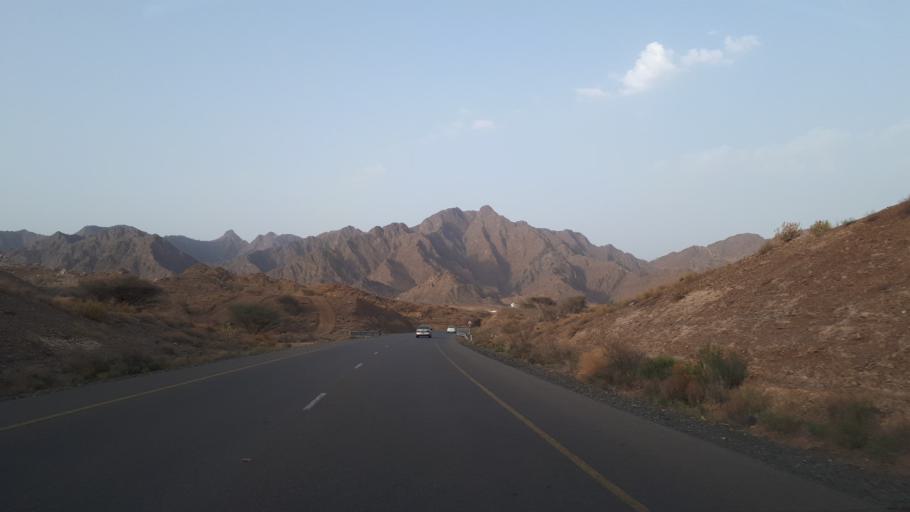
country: OM
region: Al Batinah
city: Rustaq
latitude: 23.4306
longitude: 57.1528
